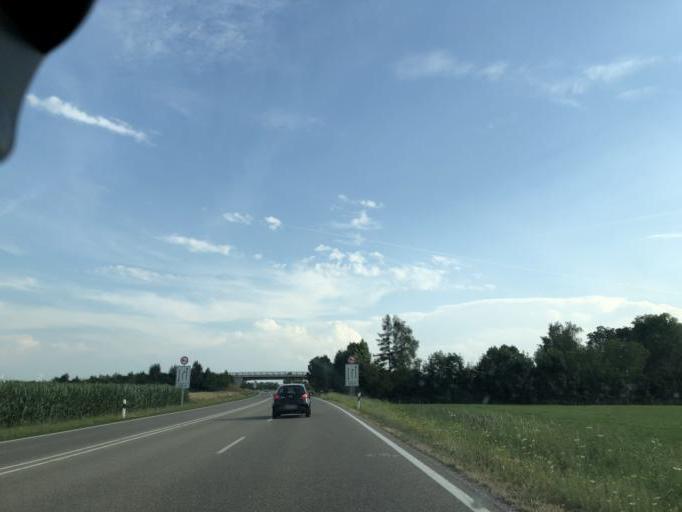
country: DE
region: Bavaria
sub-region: Swabia
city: Buchloe
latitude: 48.0194
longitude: 10.7228
